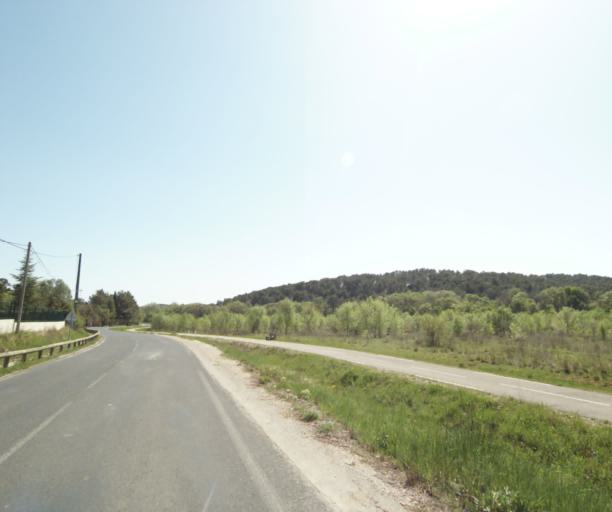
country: FR
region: Languedoc-Roussillon
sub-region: Departement de l'Herault
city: Montferrier-sur-Lez
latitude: 43.6635
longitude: 3.8460
